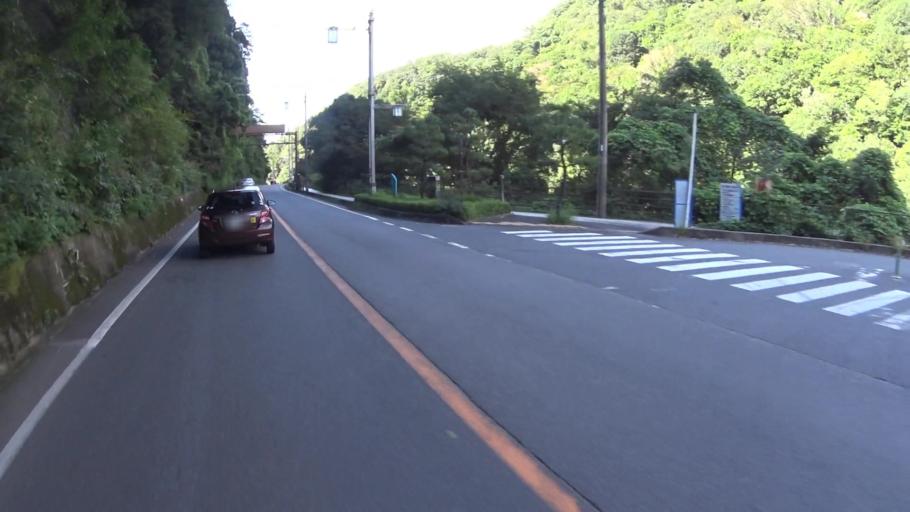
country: JP
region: Kyoto
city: Uji
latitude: 34.8834
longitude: 135.8151
